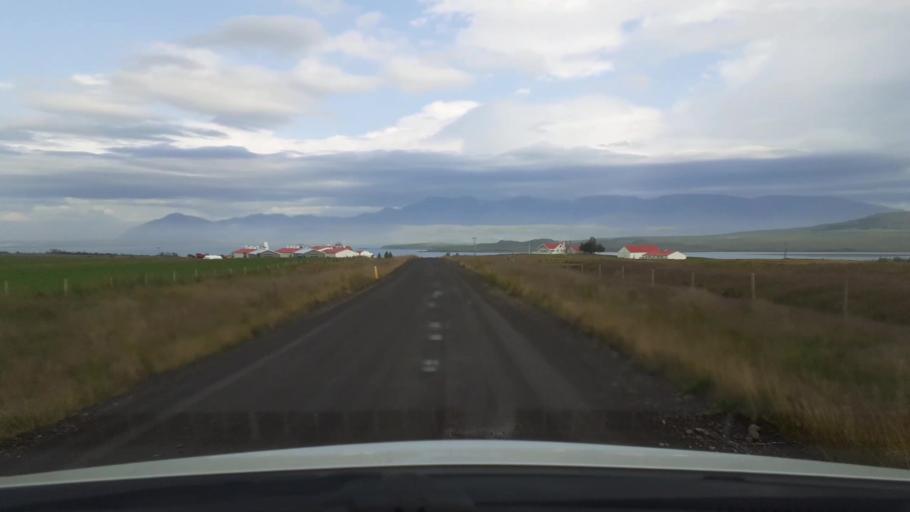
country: IS
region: Capital Region
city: Mosfellsbaer
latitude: 64.3251
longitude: -21.6504
